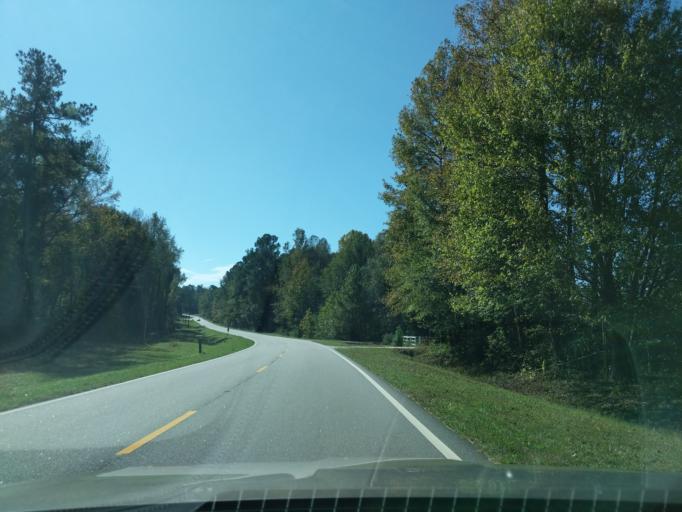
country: US
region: Georgia
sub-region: Richmond County
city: Hephzibah
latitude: 33.2918
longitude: -82.0227
